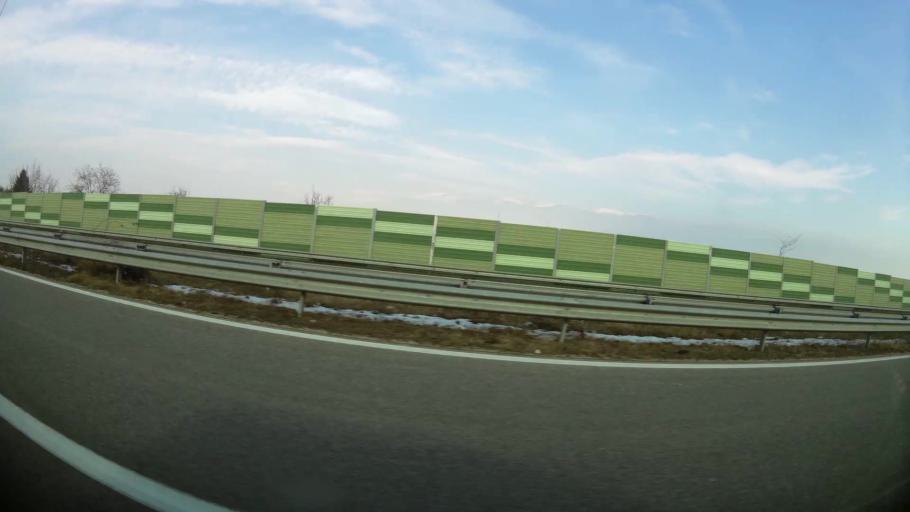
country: MK
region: Suto Orizari
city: Suto Orizare
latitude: 42.0471
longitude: 21.4379
